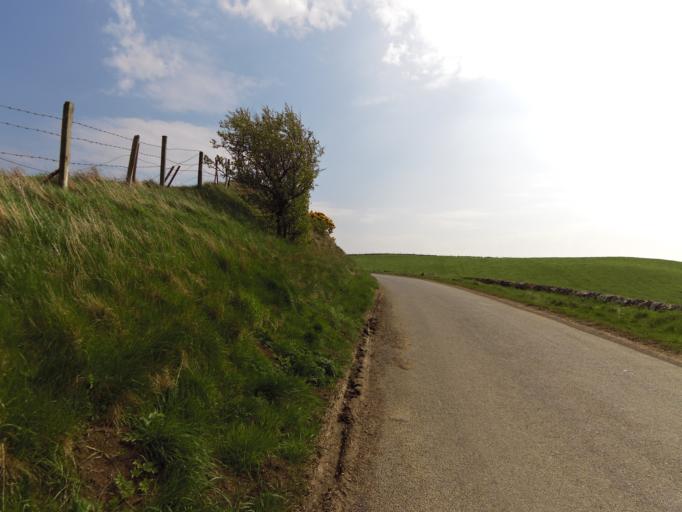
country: GB
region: Scotland
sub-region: Fife
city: Kinghorn
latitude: 56.0792
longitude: -3.1911
